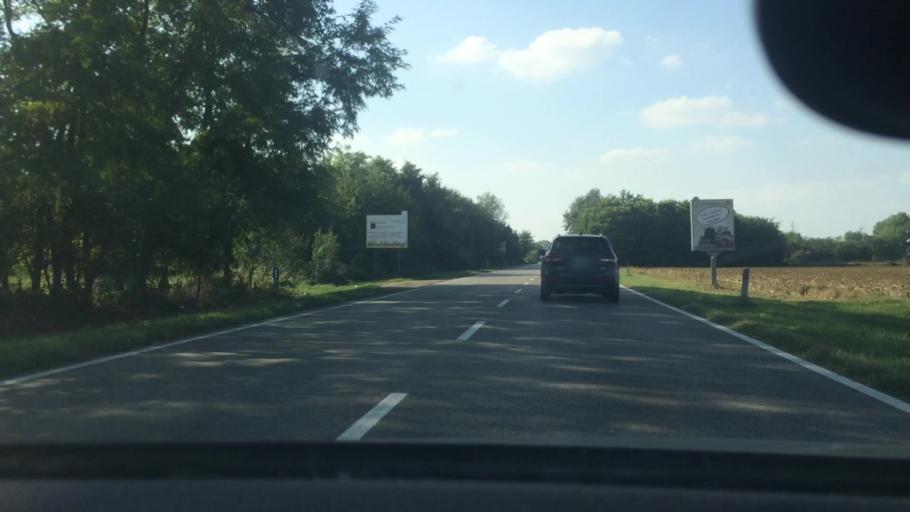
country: IT
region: Lombardy
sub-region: Citta metropolitana di Milano
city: Inveruno
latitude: 45.5265
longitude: 8.8454
